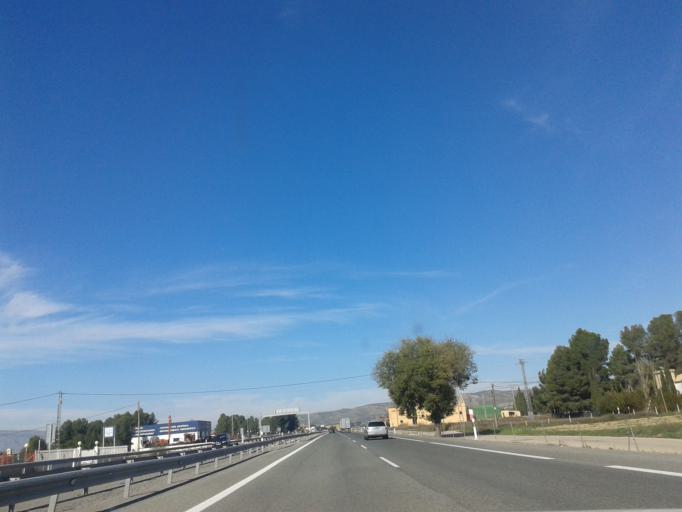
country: ES
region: Valencia
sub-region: Provincia de Alicante
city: Villena
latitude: 38.6537
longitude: -0.8744
